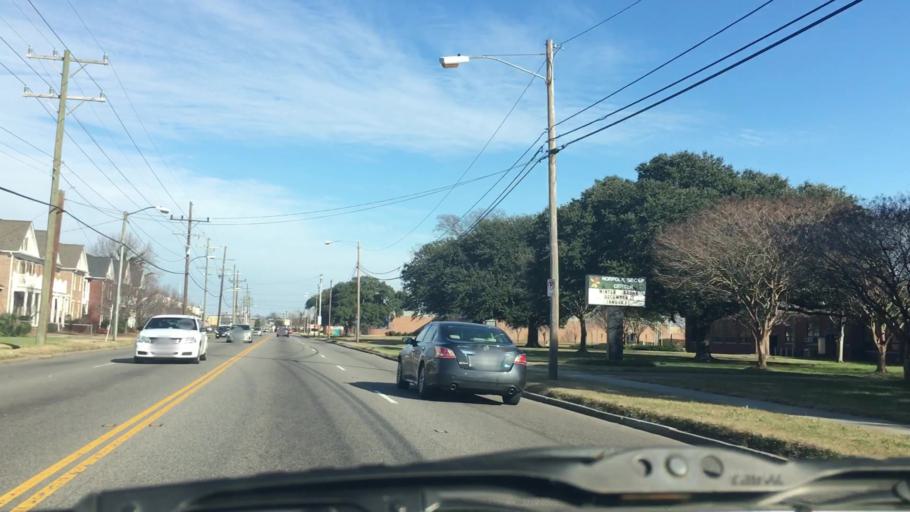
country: US
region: Virginia
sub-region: City of Norfolk
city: Norfolk
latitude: 36.8577
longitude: -76.2533
